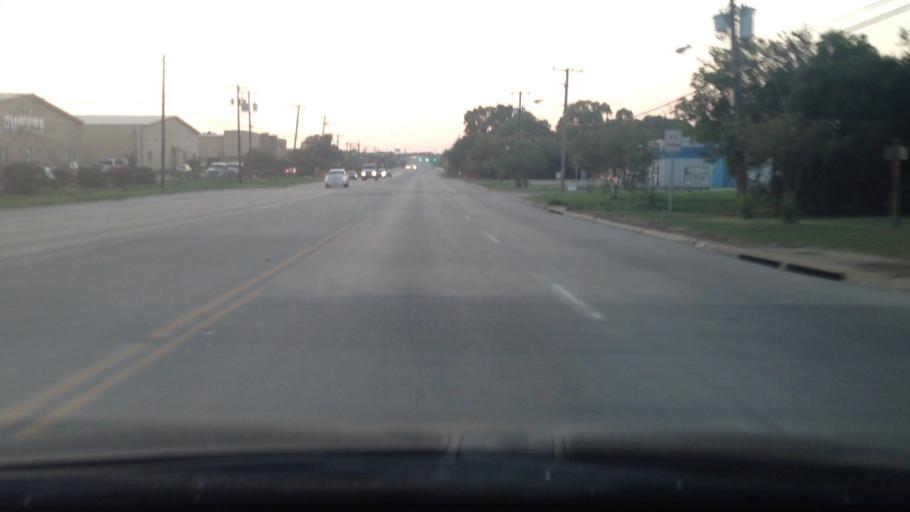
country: US
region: Texas
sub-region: Tarrant County
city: Kennedale
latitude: 32.6552
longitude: -97.2304
